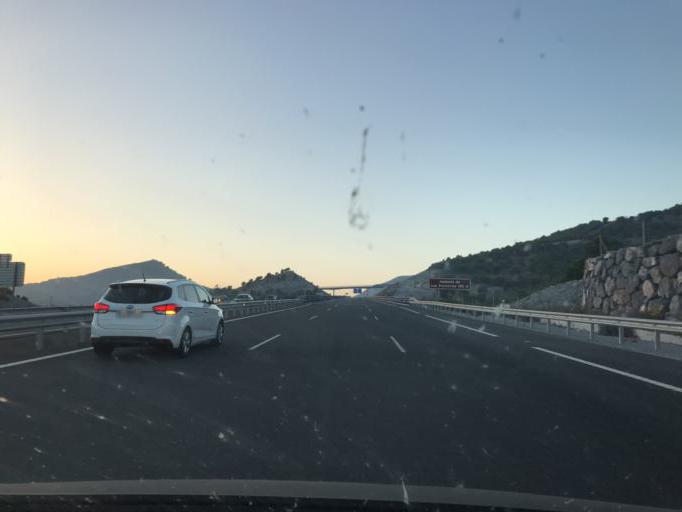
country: ES
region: Andalusia
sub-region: Provincia de Granada
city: Motril
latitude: 36.7736
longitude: -3.4921
